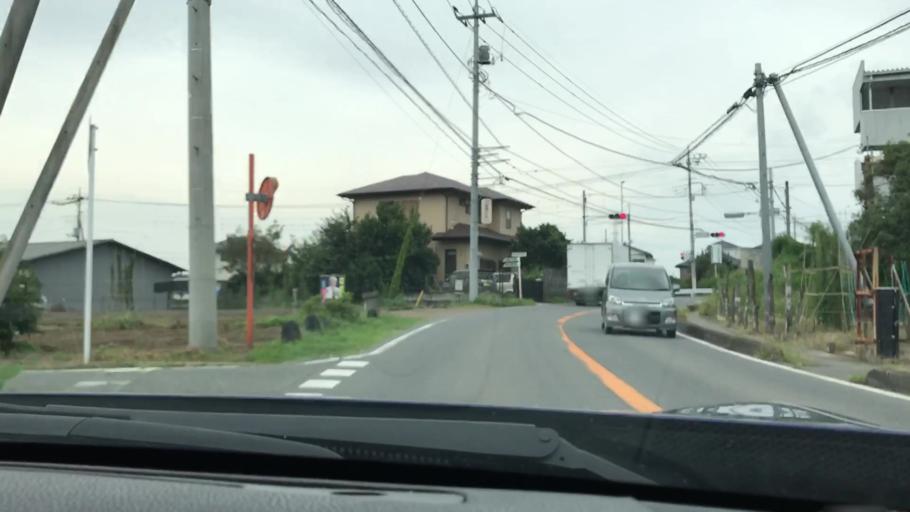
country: JP
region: Gunma
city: Kanekomachi
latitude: 36.4040
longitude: 138.9883
